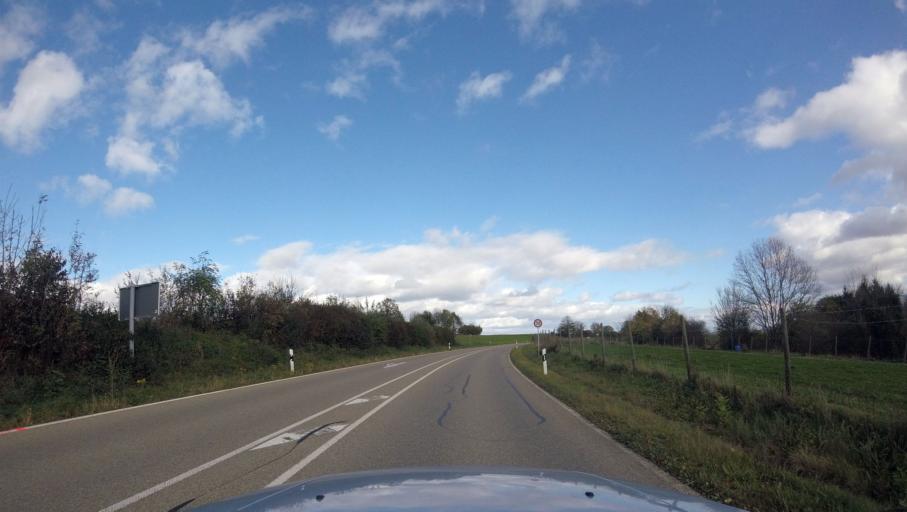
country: DE
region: Baden-Wuerttemberg
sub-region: Regierungsbezirk Stuttgart
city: Ottenbach
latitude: 48.7485
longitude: 9.7228
